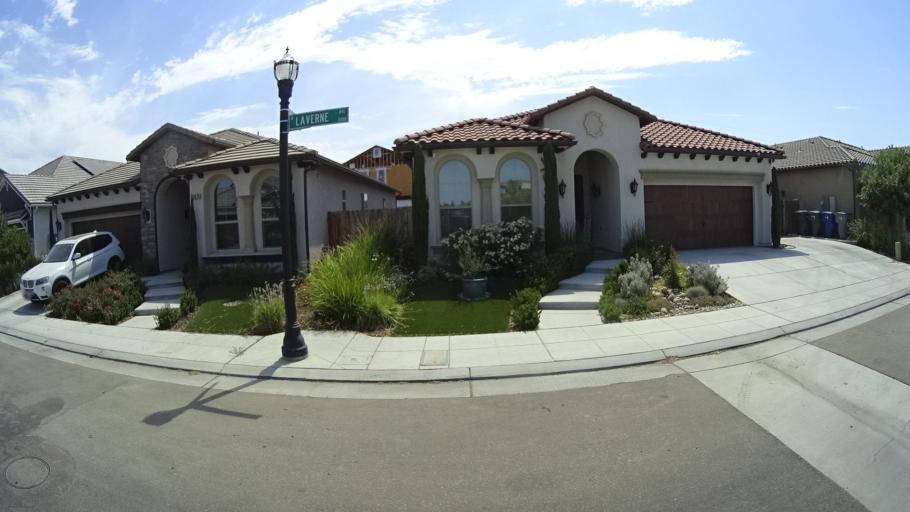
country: US
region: California
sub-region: Fresno County
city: Tarpey Village
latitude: 36.7740
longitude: -119.6781
